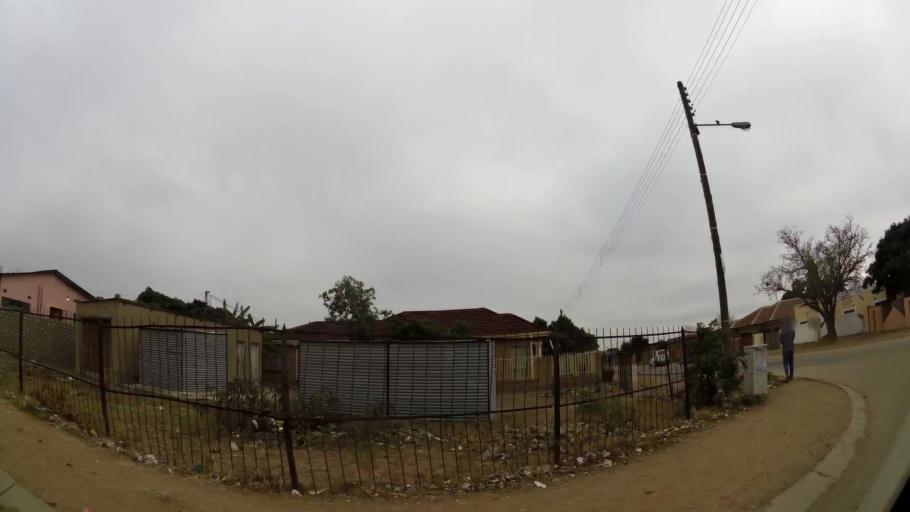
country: ZA
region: Limpopo
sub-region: Capricorn District Municipality
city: Polokwane
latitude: -23.8405
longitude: 29.3871
